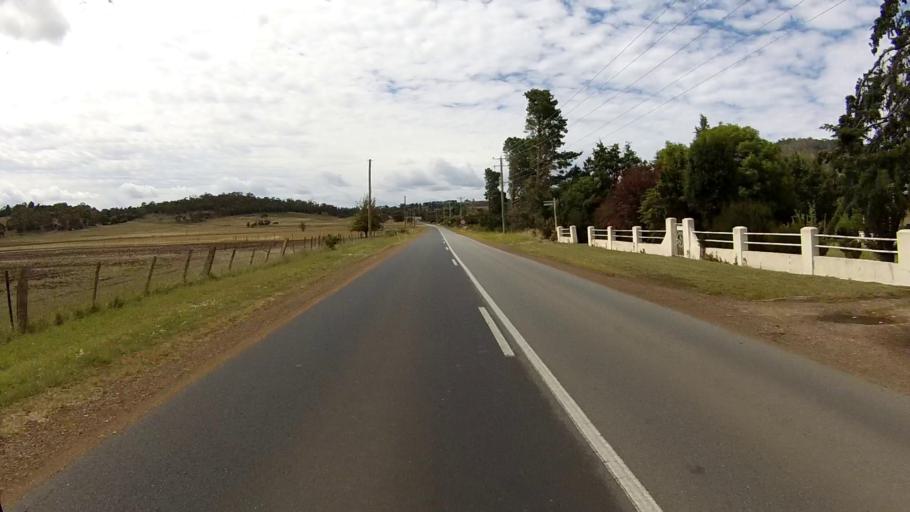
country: AU
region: Tasmania
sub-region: Clarence
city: Cambridge
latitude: -42.8139
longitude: 147.4330
